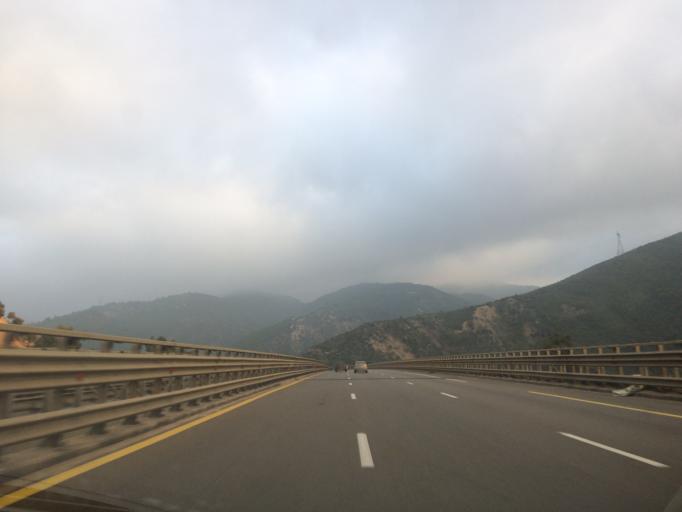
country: DZ
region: Tipaza
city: El Affroun
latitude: 36.4025
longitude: 2.5495
